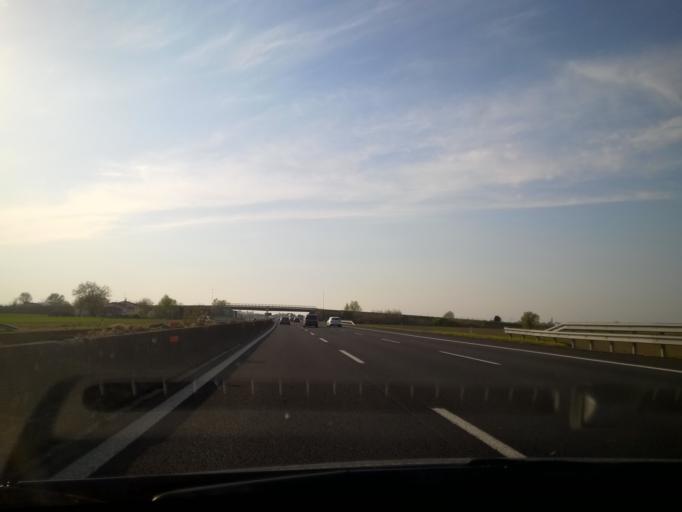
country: IT
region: Emilia-Romagna
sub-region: Provincia di Ravenna
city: Granarolo
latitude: 44.2916
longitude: 11.9866
